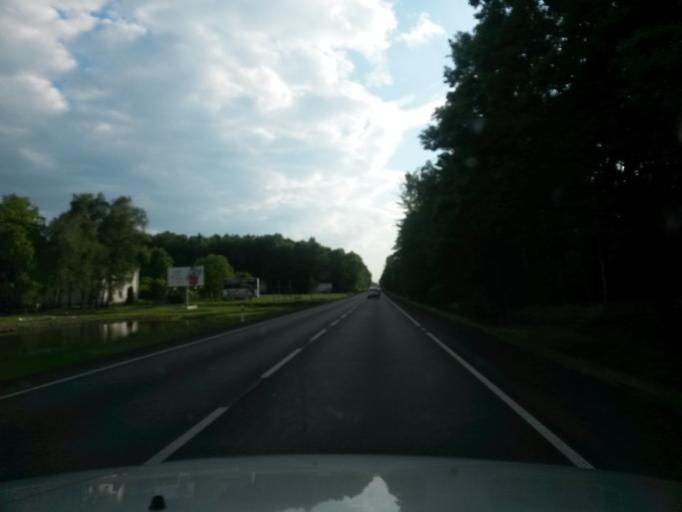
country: PL
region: Lodz Voivodeship
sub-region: Powiat belchatowski
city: Druzbice
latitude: 51.3982
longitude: 19.4274
